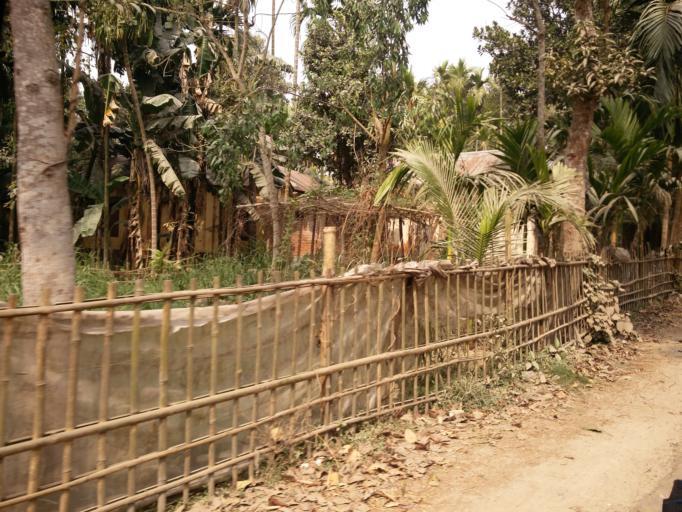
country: BD
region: Rangpur Division
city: Nageswari
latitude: 25.8848
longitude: 89.7000
